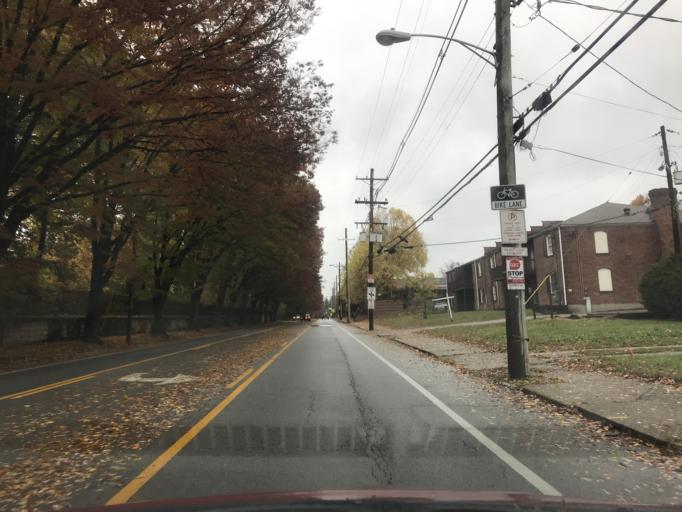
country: US
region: Kentucky
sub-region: Jefferson County
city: Audubon Park
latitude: 38.2405
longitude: -85.7150
